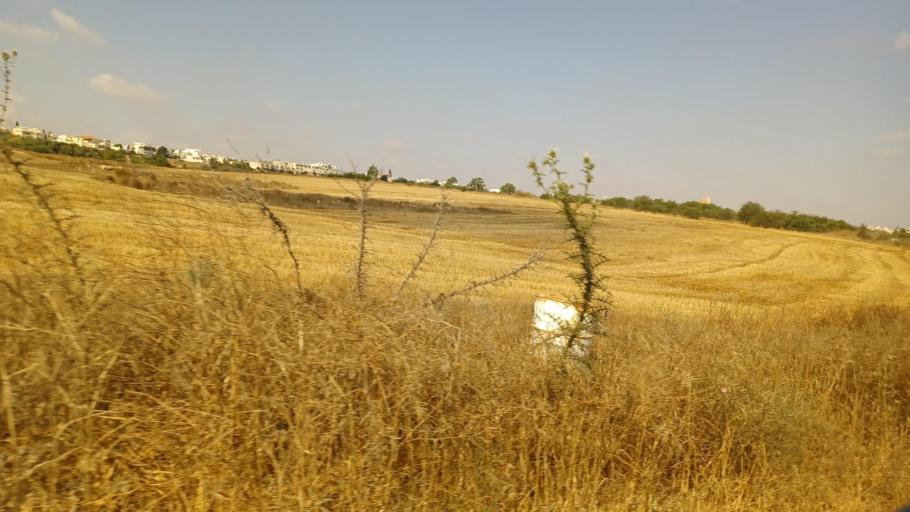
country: CY
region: Ammochostos
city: Deryneia
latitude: 35.0679
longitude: 33.9735
